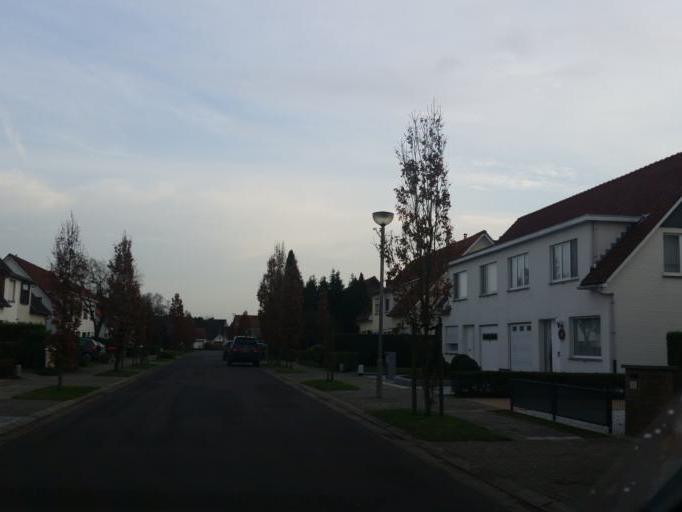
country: BE
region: Flanders
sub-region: Provincie Antwerpen
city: Sint-Katelijne-Waver
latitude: 51.0660
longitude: 4.5288
